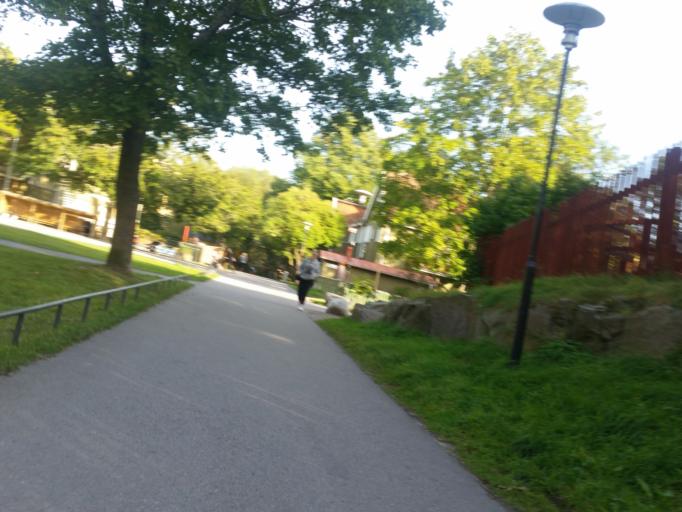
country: SE
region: Stockholm
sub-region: Stockholms Kommun
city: OEstermalm
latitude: 59.3124
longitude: 18.0931
